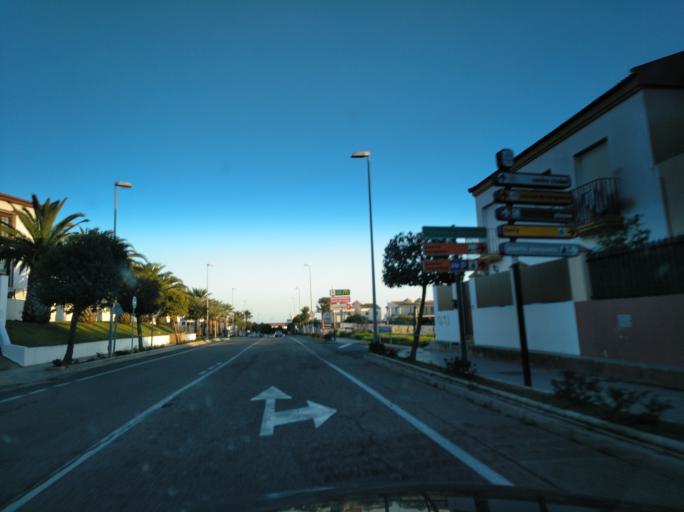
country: ES
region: Andalusia
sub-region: Provincia de Huelva
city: Ayamonte
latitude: 37.2250
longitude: -7.4030
